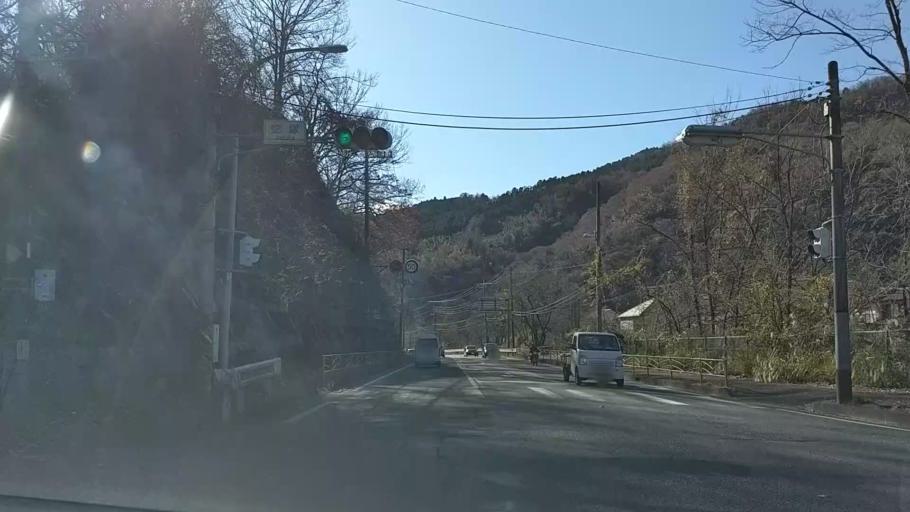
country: JP
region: Kanagawa
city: Hadano
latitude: 35.3651
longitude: 139.1596
